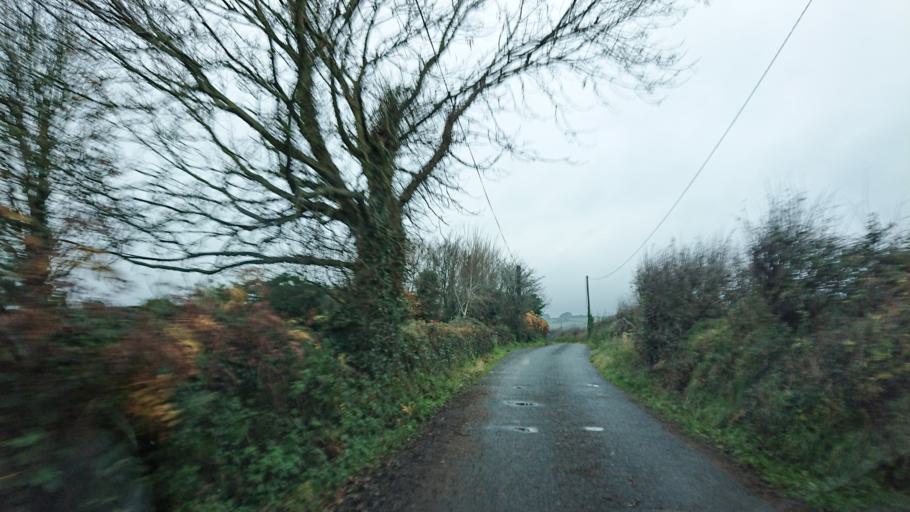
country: IE
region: Munster
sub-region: Waterford
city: Tra Mhor
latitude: 52.2001
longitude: -7.1622
